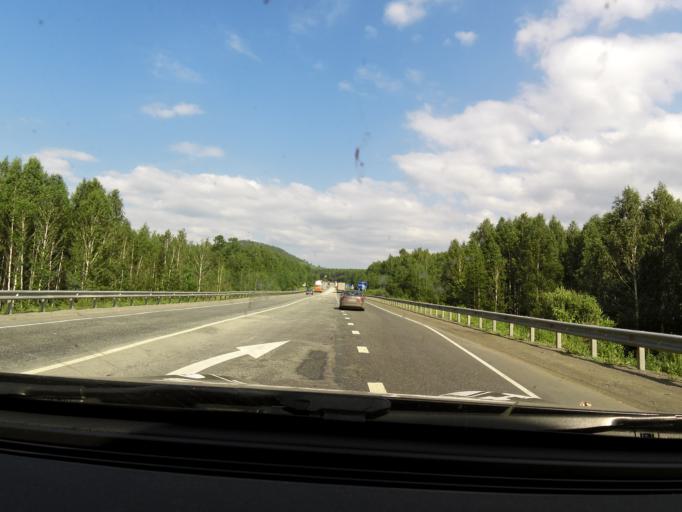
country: RU
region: Sverdlovsk
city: Revda
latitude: 56.8264
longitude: 59.9701
